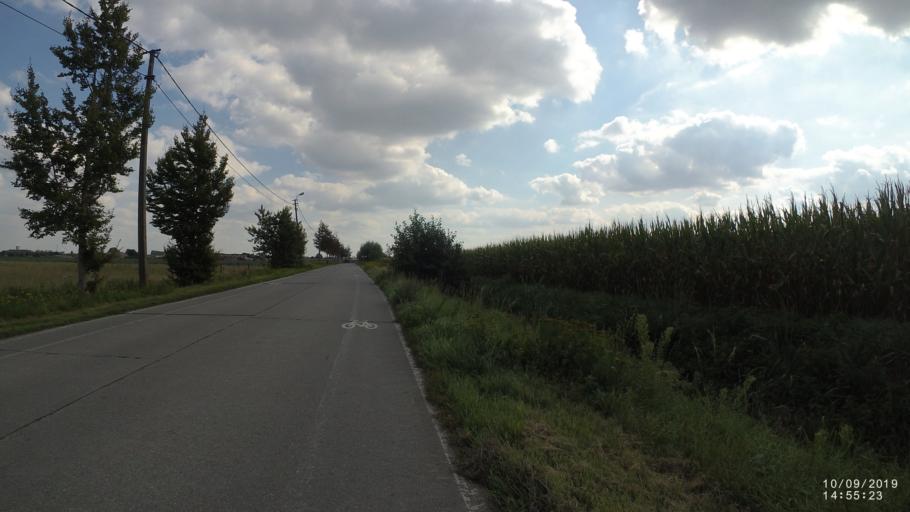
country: BE
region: Flanders
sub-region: Provincie Oost-Vlaanderen
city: Evergem
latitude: 51.1394
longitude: 3.6979
